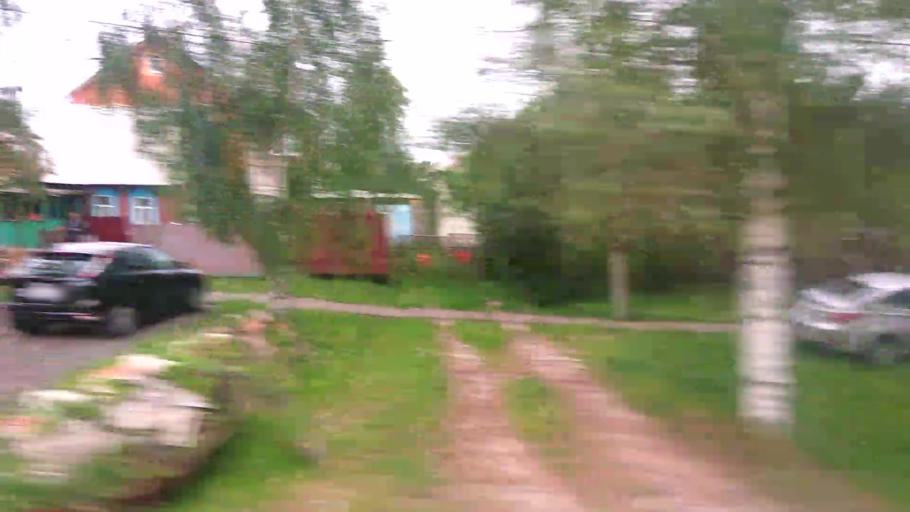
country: RU
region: Moskovskaya
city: Lukhovitsy
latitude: 54.9325
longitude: 39.0038
